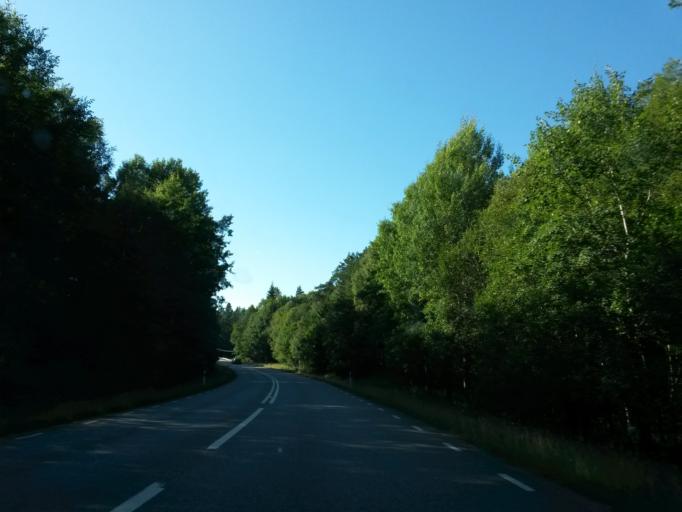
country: SE
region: Vaestra Goetaland
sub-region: Vargarda Kommun
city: Vargarda
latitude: 57.9403
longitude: 12.8488
